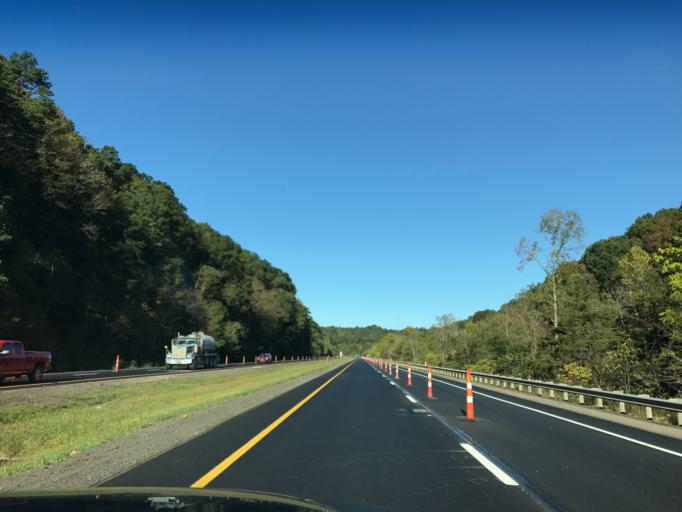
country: US
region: Ohio
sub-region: Washington County
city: Reno
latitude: 39.2448
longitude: -81.3714
